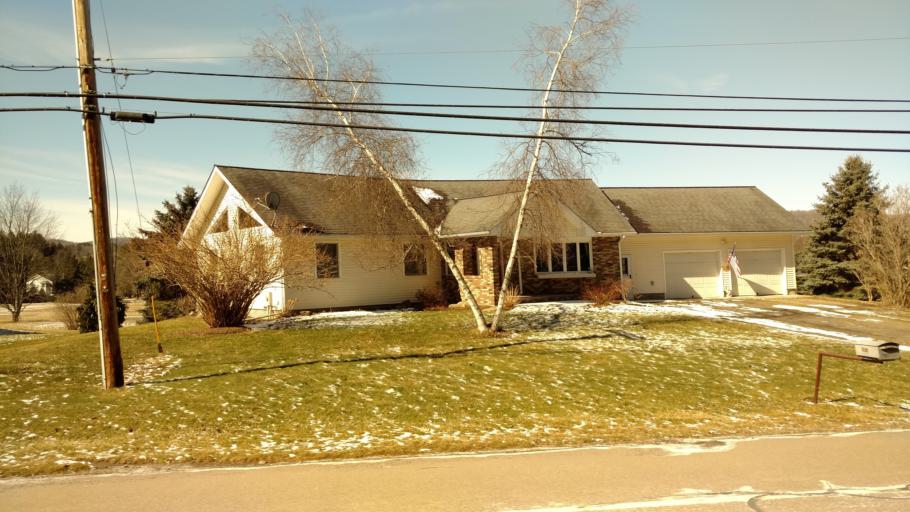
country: US
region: New York
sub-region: Allegany County
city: Wellsville
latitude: 42.0805
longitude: -77.9210
